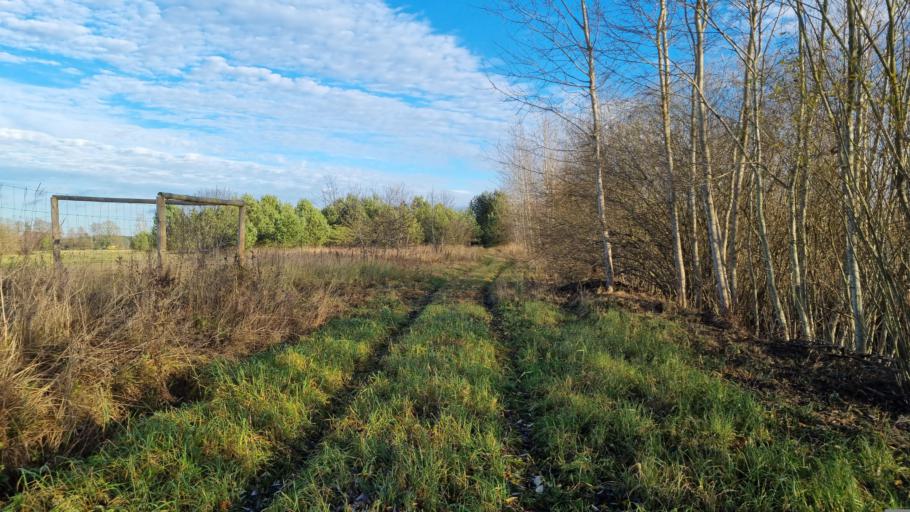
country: LV
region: Kekava
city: Kekava
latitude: 56.8134
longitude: 24.1970
